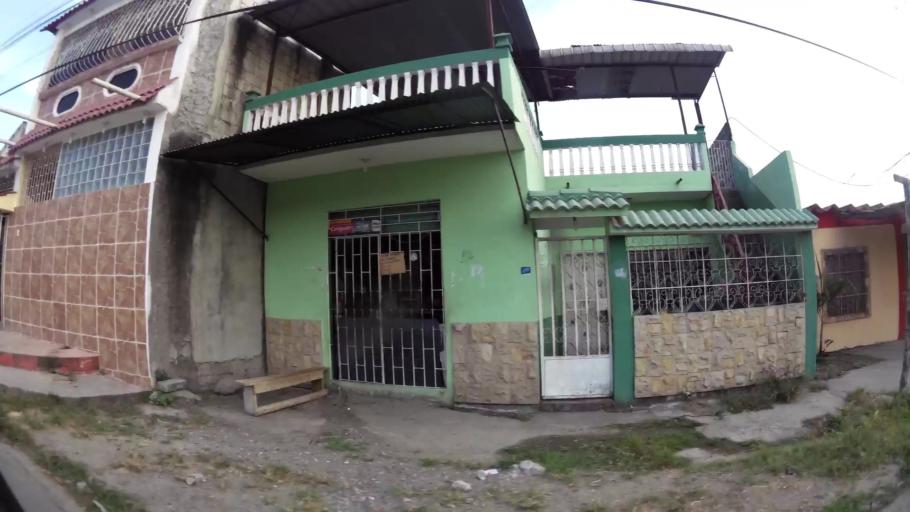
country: EC
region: Guayas
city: Eloy Alfaro
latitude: -2.0953
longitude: -79.9031
